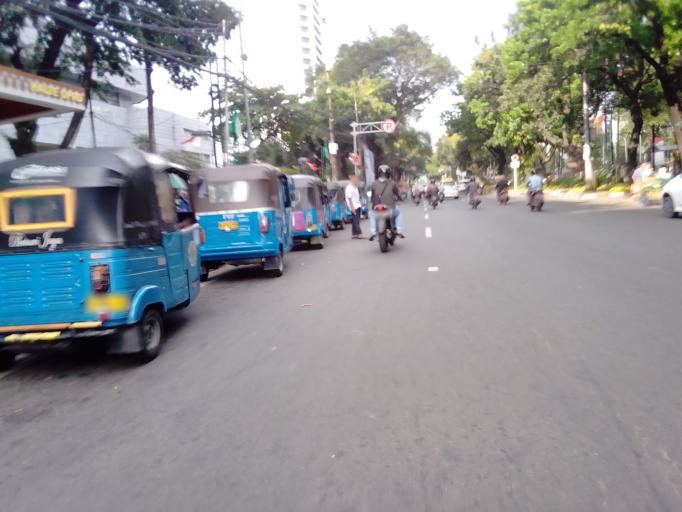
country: ID
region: Jakarta Raya
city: Jakarta
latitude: -6.1828
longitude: 106.8284
